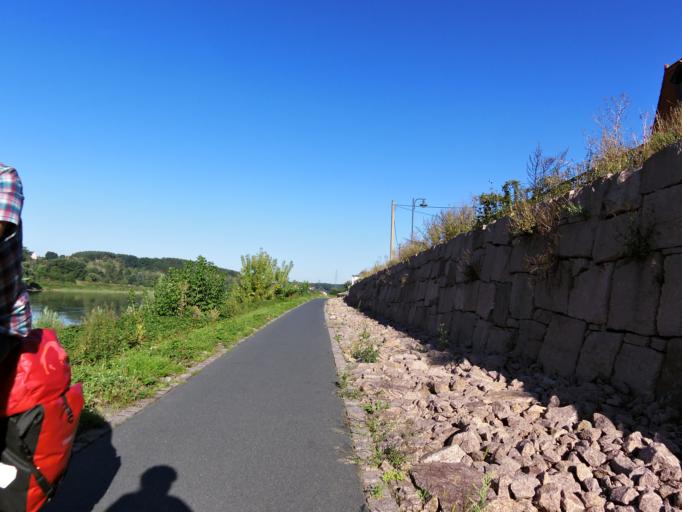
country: DE
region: Saxony
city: Weissig
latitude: 51.2353
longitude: 13.4226
